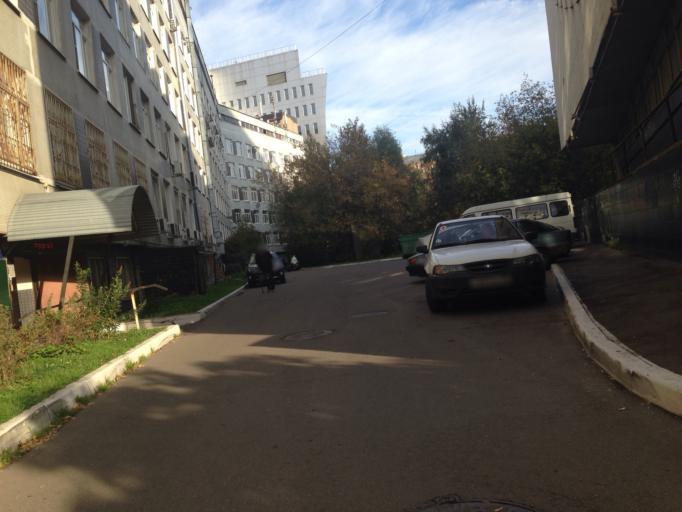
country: RU
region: Moscow
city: Mar'ina Roshcha
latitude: 55.7873
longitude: 37.6256
